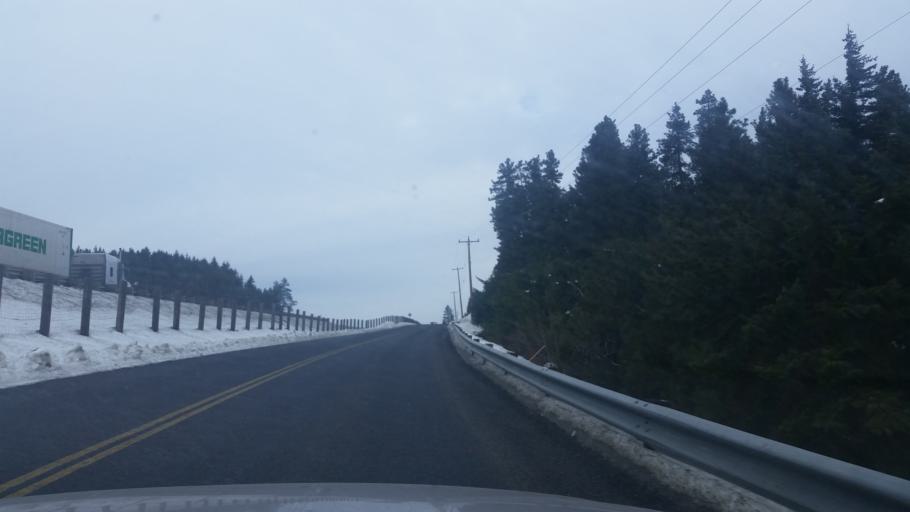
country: US
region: Washington
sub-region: Kittitas County
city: Cle Elum
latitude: 47.1233
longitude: -120.8007
